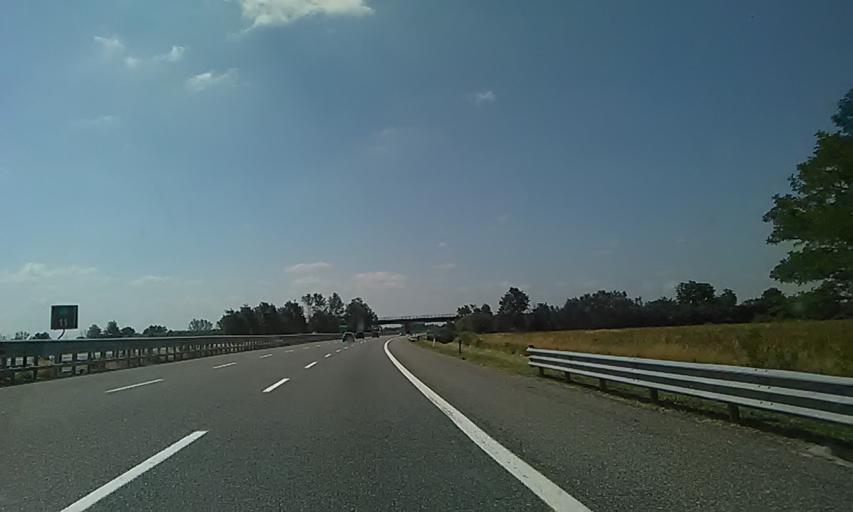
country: IT
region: Piedmont
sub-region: Provincia di Alessandria
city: Castellazzo Bormida
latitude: 44.8438
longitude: 8.5959
